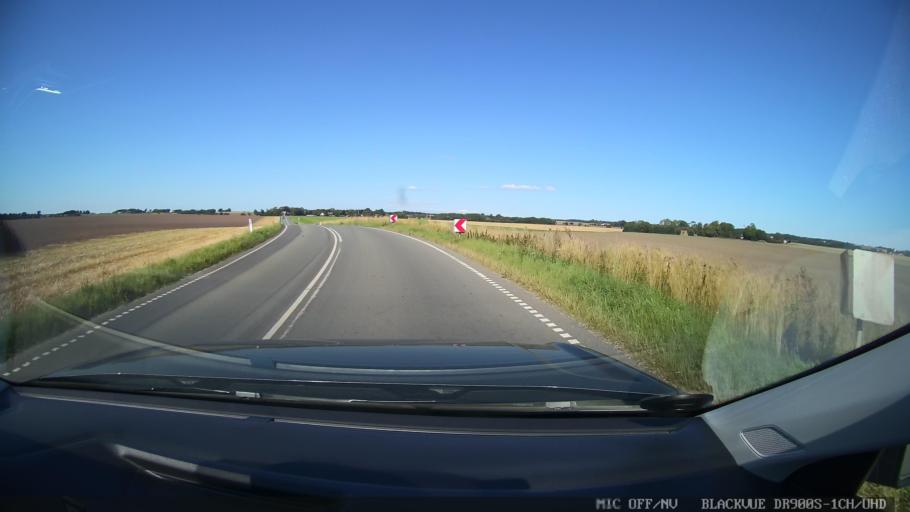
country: DK
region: Central Jutland
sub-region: Randers Kommune
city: Spentrup
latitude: 56.5458
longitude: 10.0012
